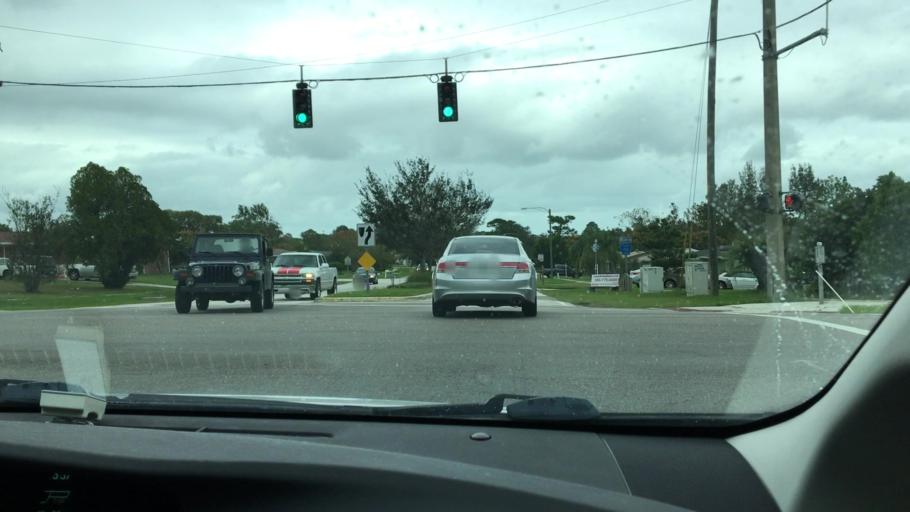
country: US
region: Florida
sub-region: Volusia County
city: Deltona
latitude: 28.8916
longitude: -81.2321
